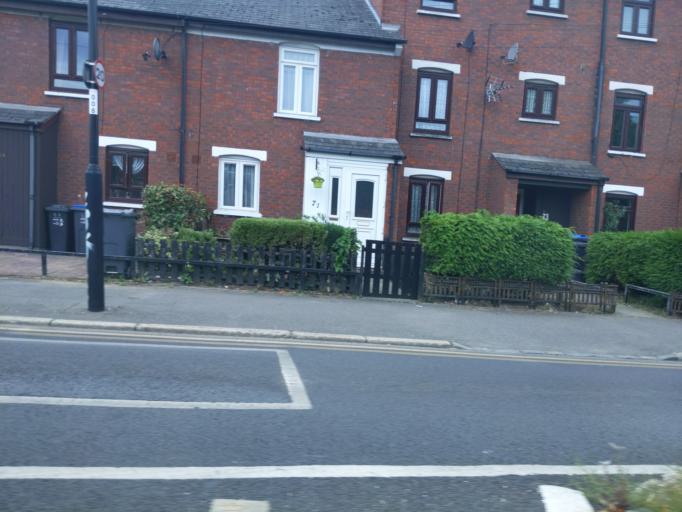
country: GB
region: England
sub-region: Greater London
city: Croydon
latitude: 51.3874
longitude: -0.1023
